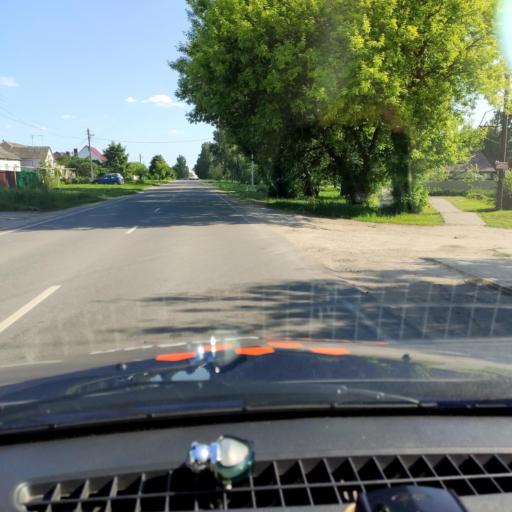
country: RU
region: Voronezj
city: Podgornoye
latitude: 51.8843
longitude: 39.1726
